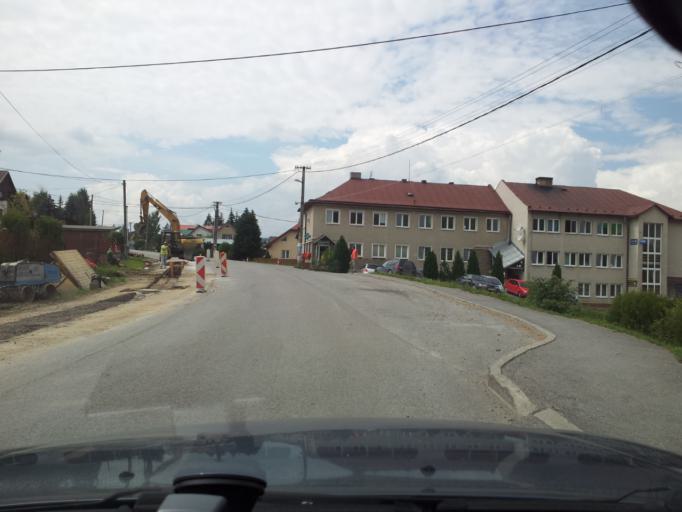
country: SK
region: Zilinsky
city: Oravska Lesna
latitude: 49.3859
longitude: 19.3018
